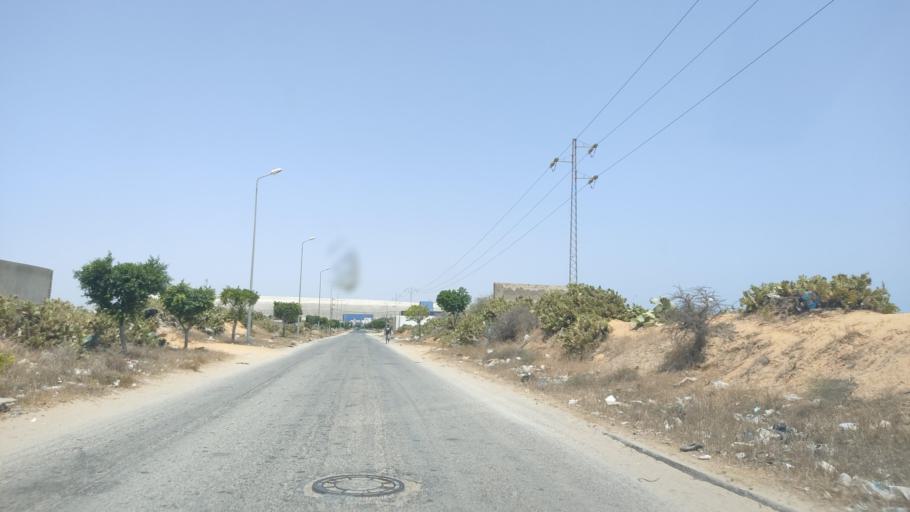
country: TN
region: Safaqis
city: Sfax
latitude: 34.6856
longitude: 10.7236
